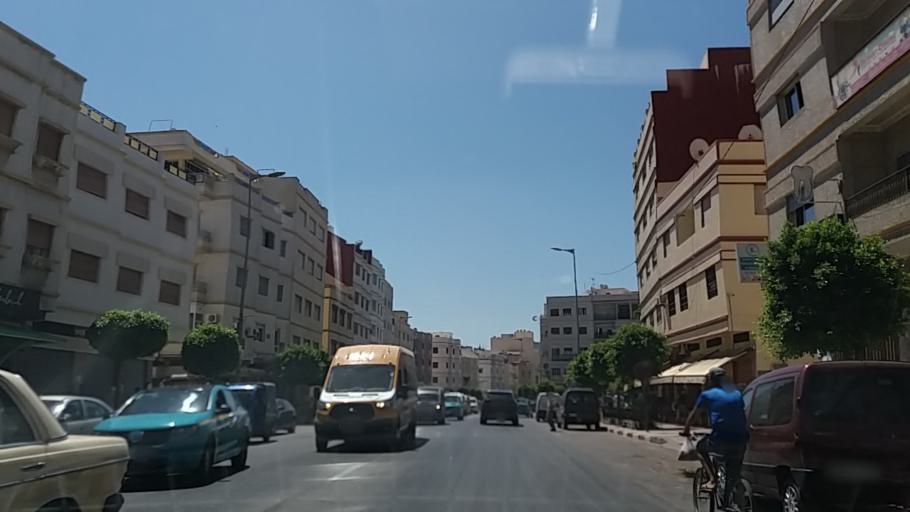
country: MA
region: Tanger-Tetouan
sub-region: Tanger-Assilah
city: Tangier
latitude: 35.7593
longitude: -5.8019
